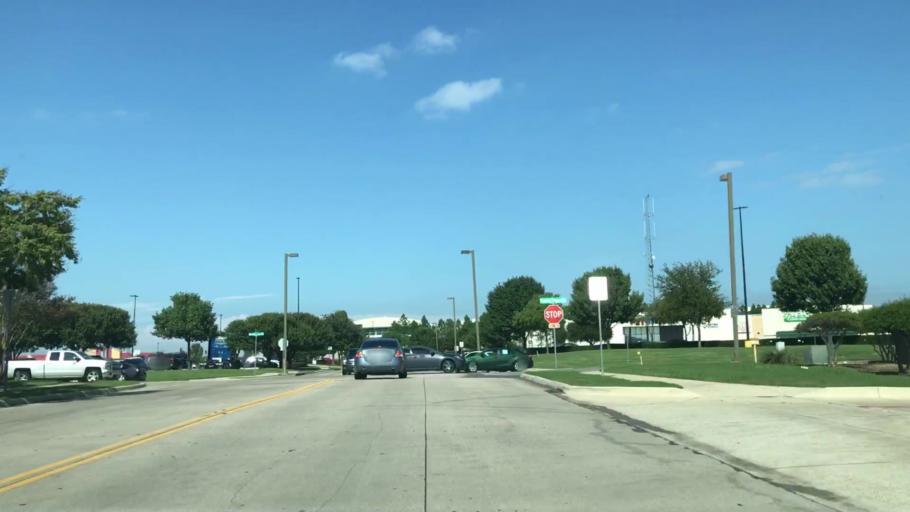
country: US
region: Texas
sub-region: Dallas County
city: Coppell
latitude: 32.9183
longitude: -96.9659
